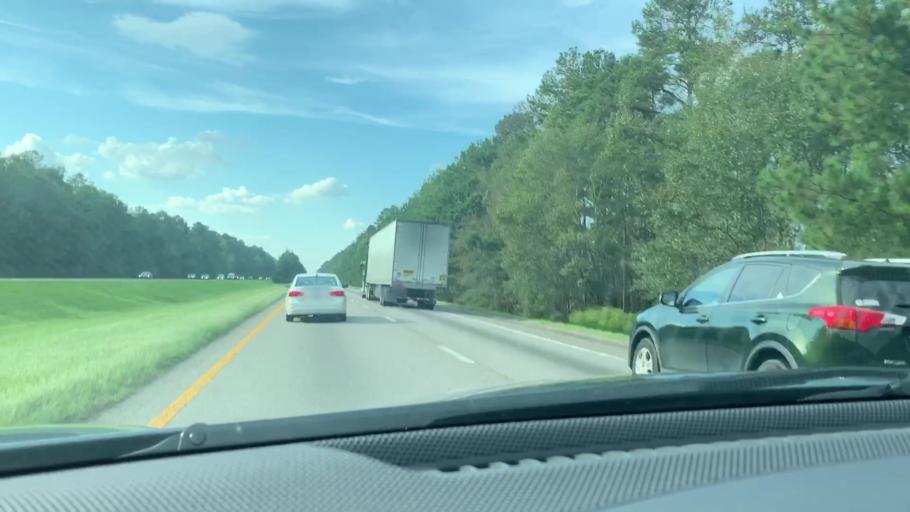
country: US
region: South Carolina
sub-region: Orangeburg County
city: Brookdale
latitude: 33.4328
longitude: -80.6950
